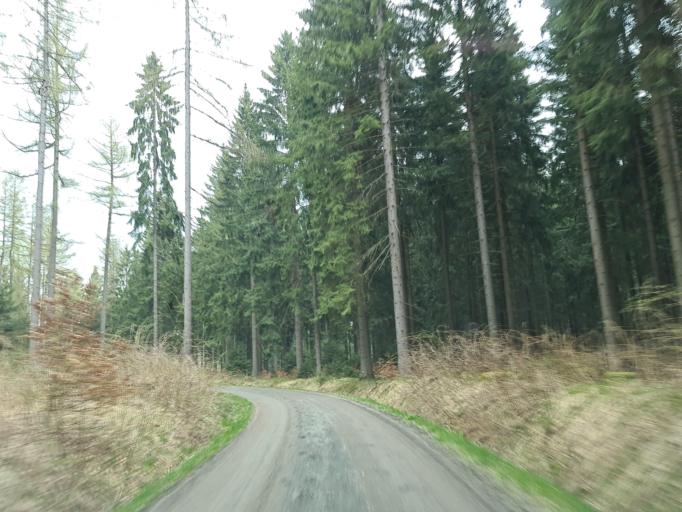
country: DE
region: Saxony
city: Ellefeld
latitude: 50.4593
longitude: 12.3989
